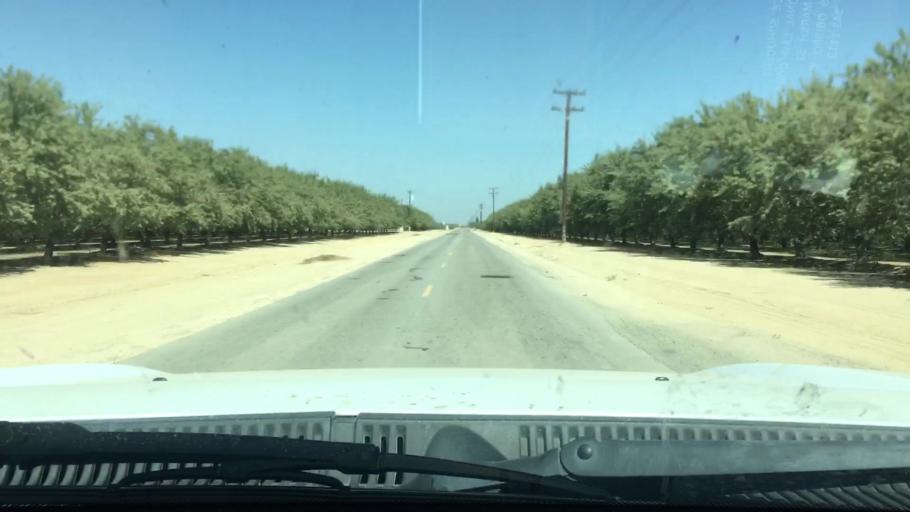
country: US
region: California
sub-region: Kern County
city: Shafter
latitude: 35.4123
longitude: -119.2875
